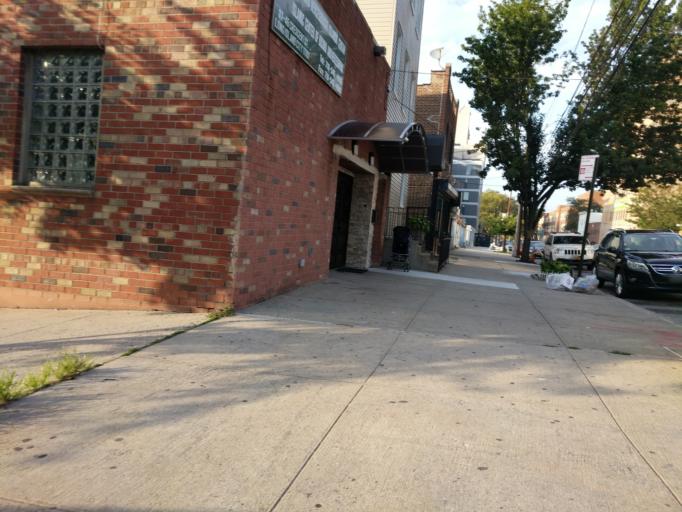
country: US
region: New York
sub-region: Queens County
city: Long Island City
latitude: 40.7559
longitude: -73.9358
